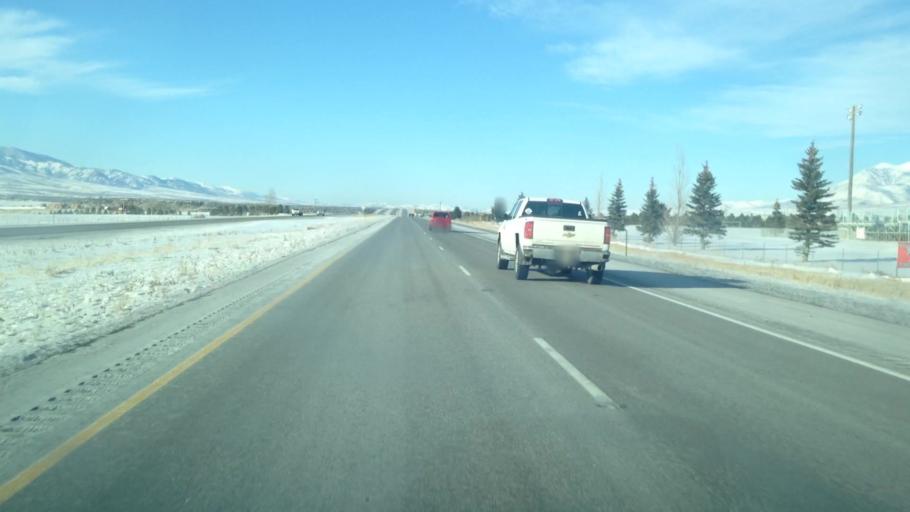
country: US
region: Idaho
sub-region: Oneida County
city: Malad City
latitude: 42.5784
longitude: -112.1831
